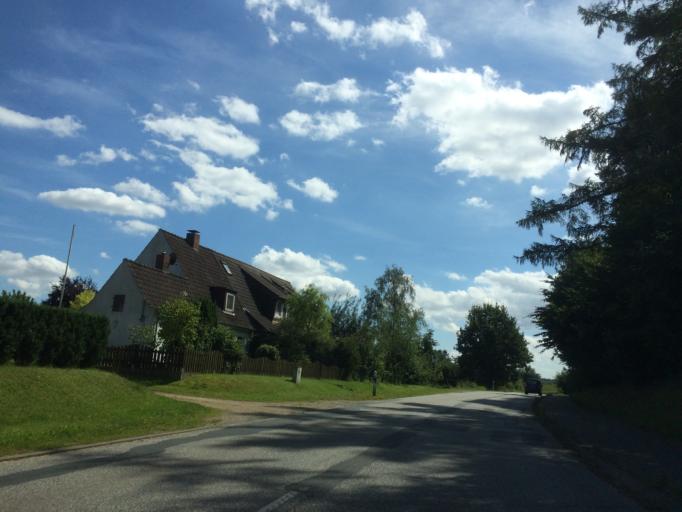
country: DE
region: Schleswig-Holstein
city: Grebin
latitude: 54.2013
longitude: 10.4741
